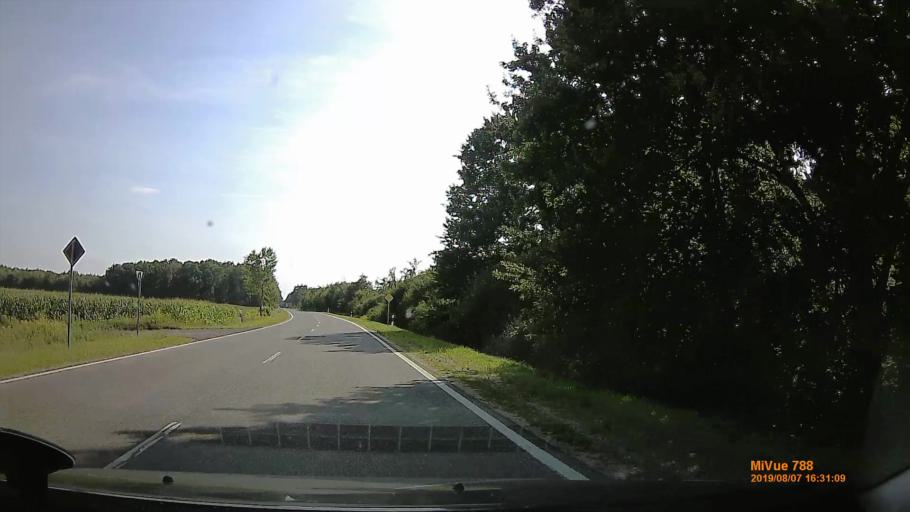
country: HU
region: Zala
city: Lenti
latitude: 46.6606
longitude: 16.5029
